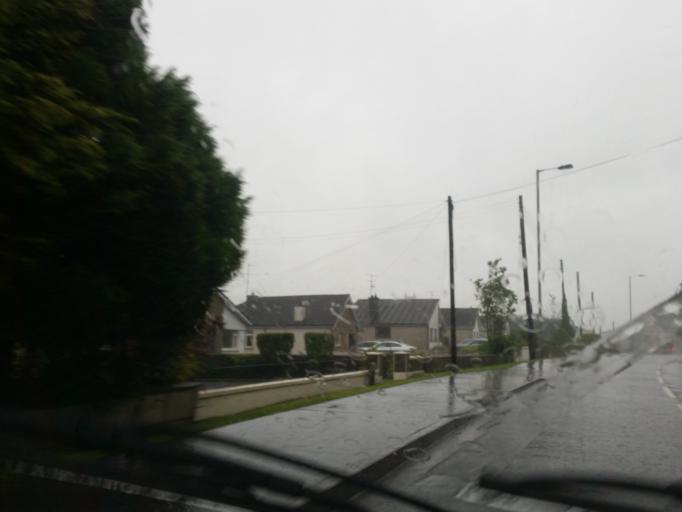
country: GB
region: Northern Ireland
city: Fivemiletown
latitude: 54.4136
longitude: -7.1662
